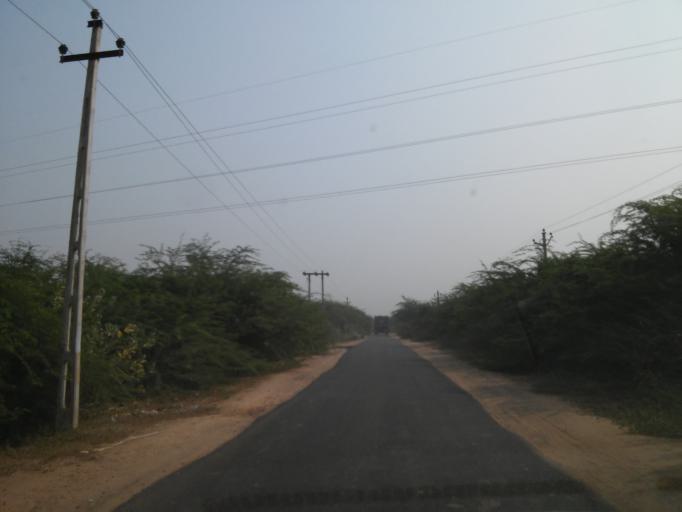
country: IN
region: Gujarat
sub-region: Kachchh
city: Bhuj
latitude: 23.4298
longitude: 69.6855
